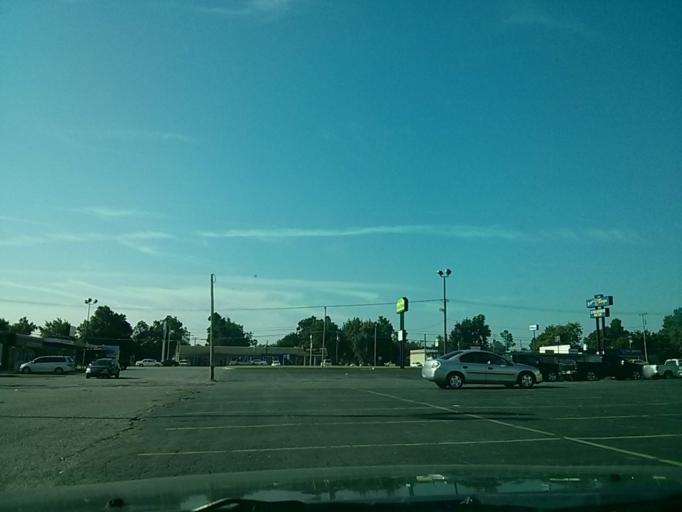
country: US
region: Oklahoma
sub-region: Tulsa County
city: Tulsa
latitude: 36.1619
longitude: -95.8986
